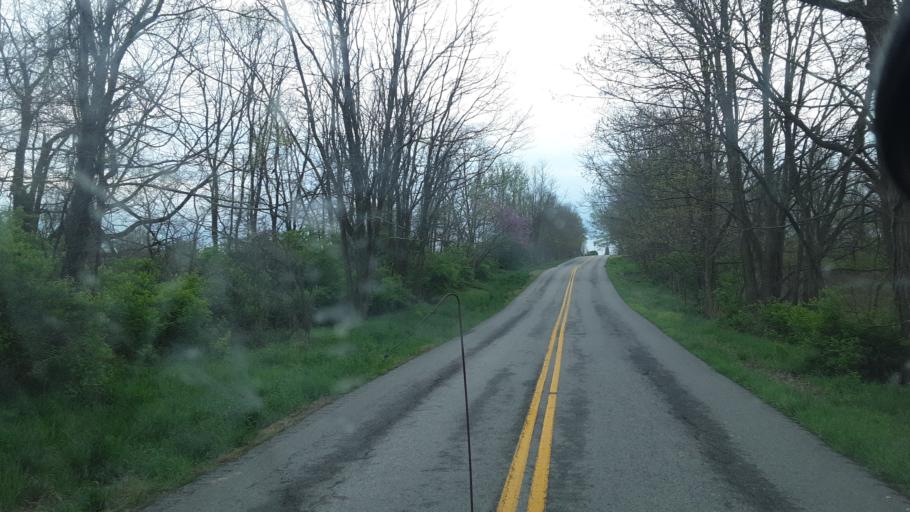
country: US
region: Kentucky
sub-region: Owen County
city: Owenton
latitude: 38.6211
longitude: -84.7863
